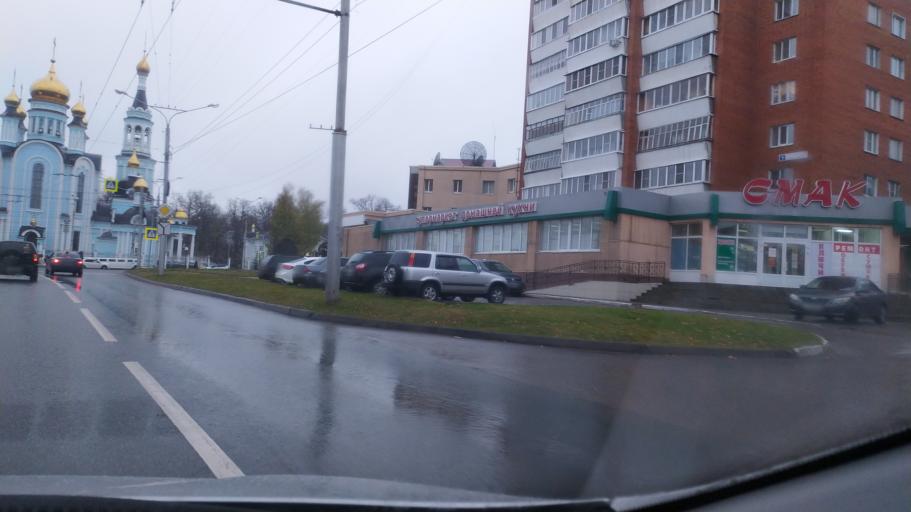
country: RU
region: Chuvashia
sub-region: Cheboksarskiy Rayon
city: Cheboksary
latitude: 56.1419
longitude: 47.1860
